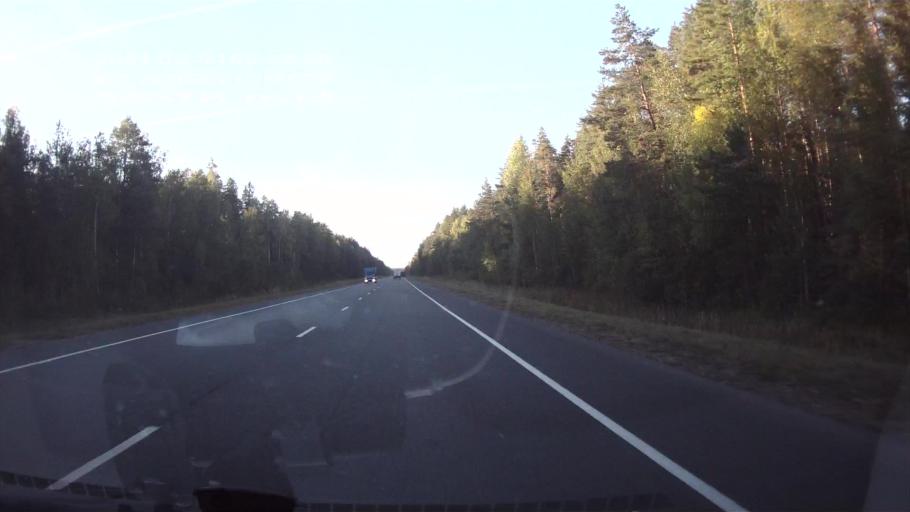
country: RU
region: Chuvashia
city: Mariinskiy Posad
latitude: 56.2557
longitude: 47.8066
